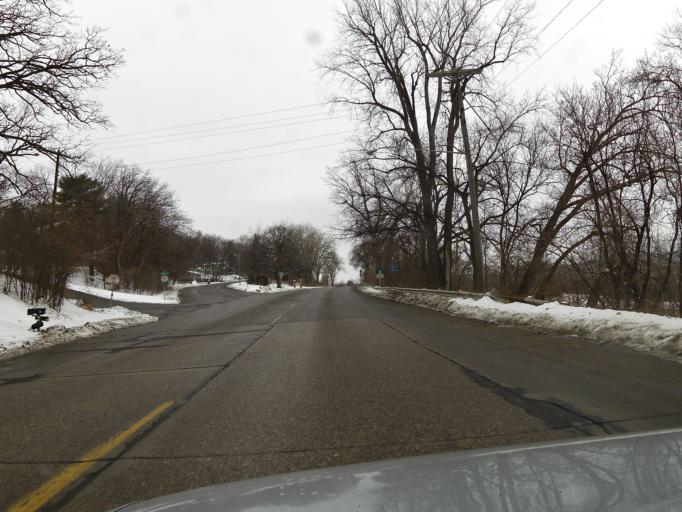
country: US
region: Minnesota
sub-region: Dakota County
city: South Saint Paul
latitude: 44.9192
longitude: -93.0593
